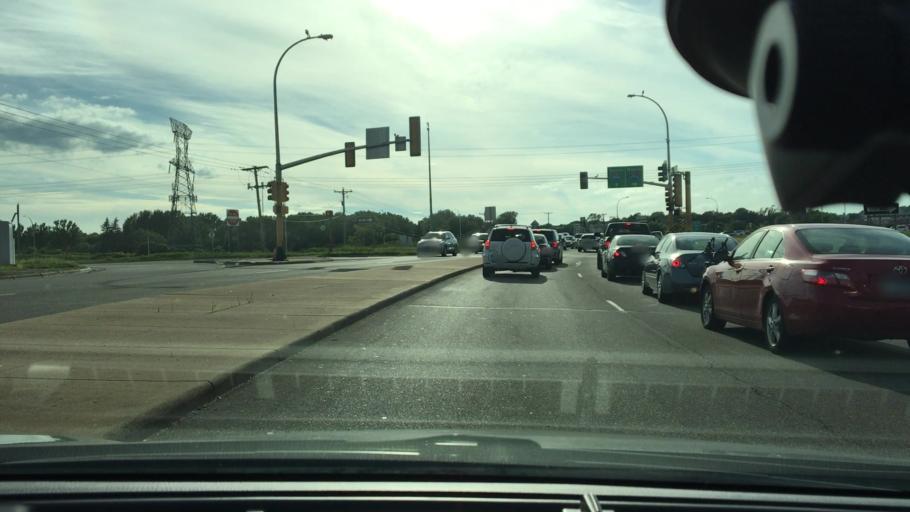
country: US
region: Minnesota
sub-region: Hennepin County
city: Plymouth
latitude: 45.0281
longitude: -93.4508
